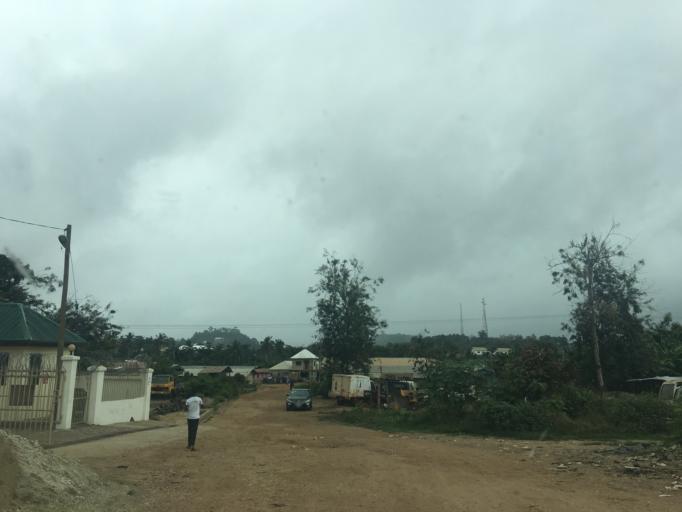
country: GH
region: Western
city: Wassa-Akropong
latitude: 5.8167
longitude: -2.4336
